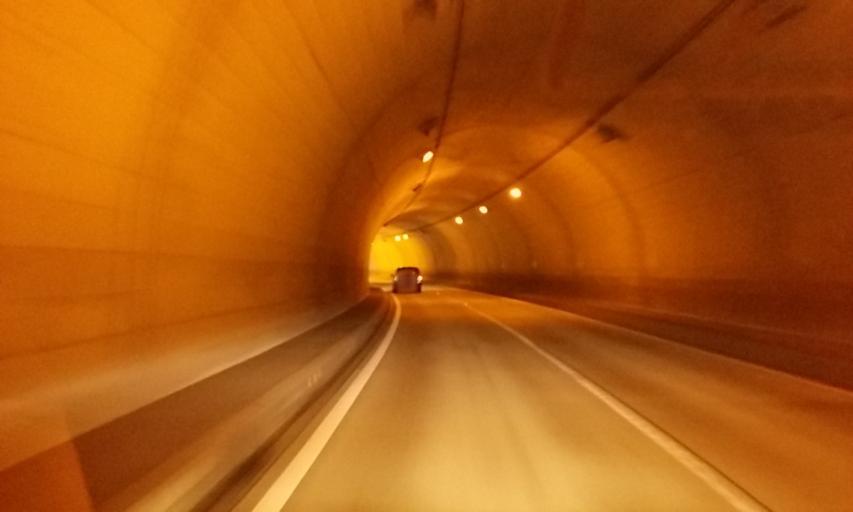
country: JP
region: Kyoto
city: Miyazu
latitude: 35.5824
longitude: 135.1168
